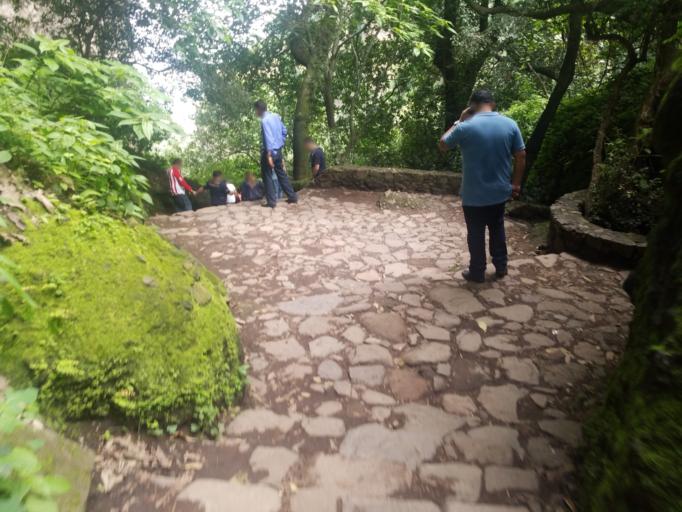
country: MX
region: Morelos
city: Tepoztlan
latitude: 18.9997
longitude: -99.1016
